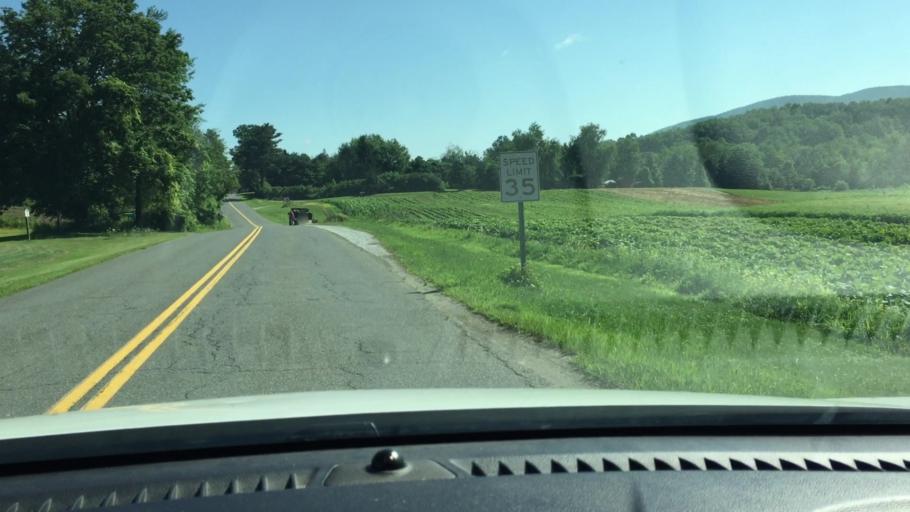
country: US
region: Massachusetts
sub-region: Berkshire County
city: Lanesborough
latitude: 42.5133
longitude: -73.2178
